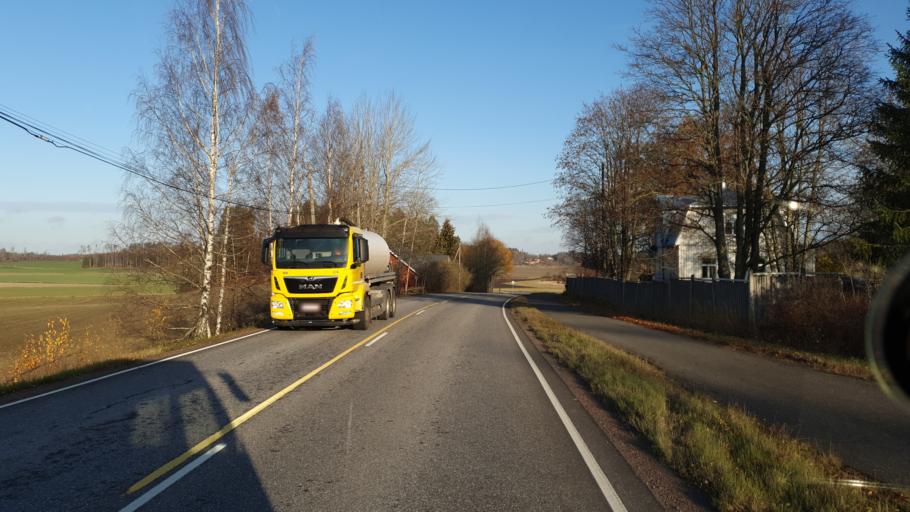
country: FI
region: Uusimaa
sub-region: Helsinki
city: Siuntio
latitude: 60.1552
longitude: 24.2068
